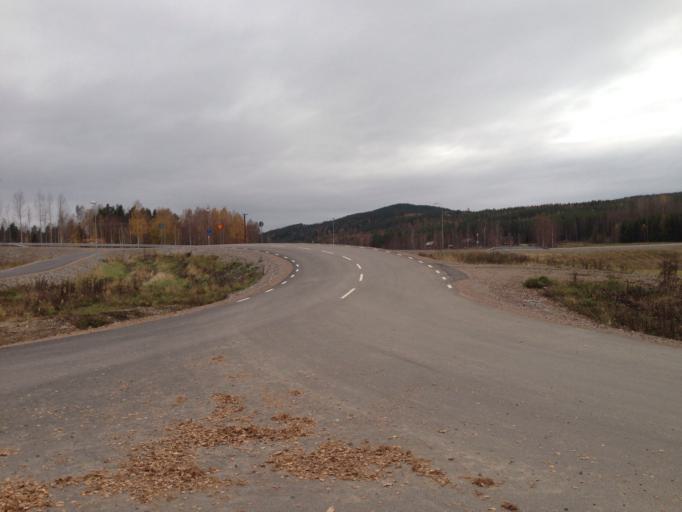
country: SE
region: Gaevleborg
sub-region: Bollnas Kommun
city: Bollnas
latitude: 61.3516
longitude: 16.3476
